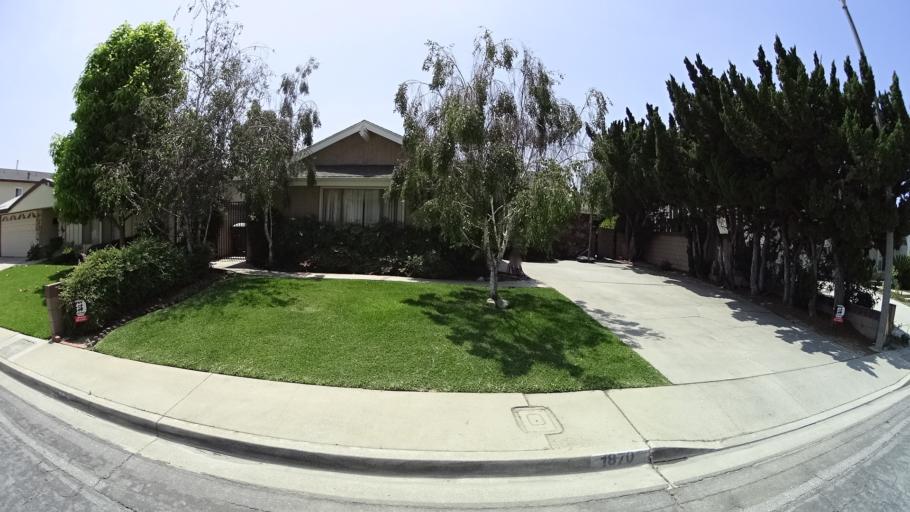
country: US
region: California
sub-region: Los Angeles County
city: Belvedere
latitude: 34.0541
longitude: -118.1550
